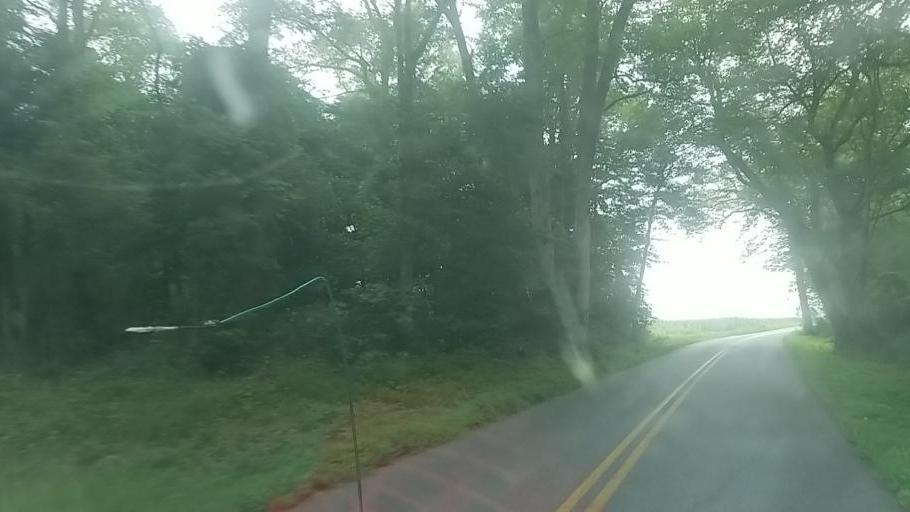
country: US
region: Delaware
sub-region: Sussex County
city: Selbyville
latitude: 38.4254
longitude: -75.3025
